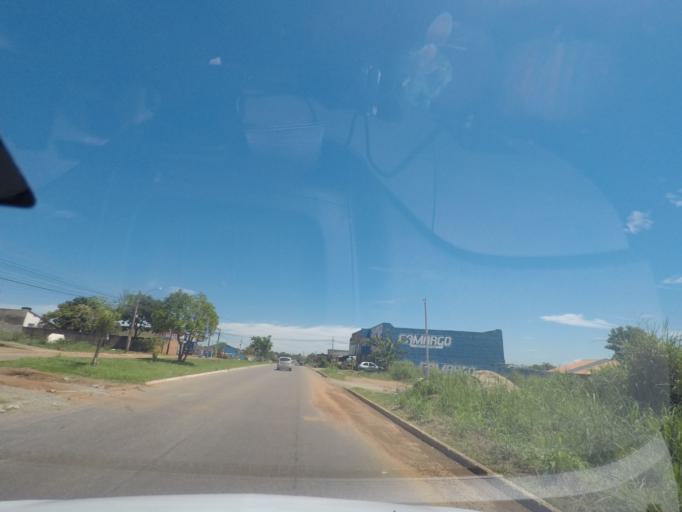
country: BR
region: Goias
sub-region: Aparecida De Goiania
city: Aparecida de Goiania
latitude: -16.7813
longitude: -49.3262
